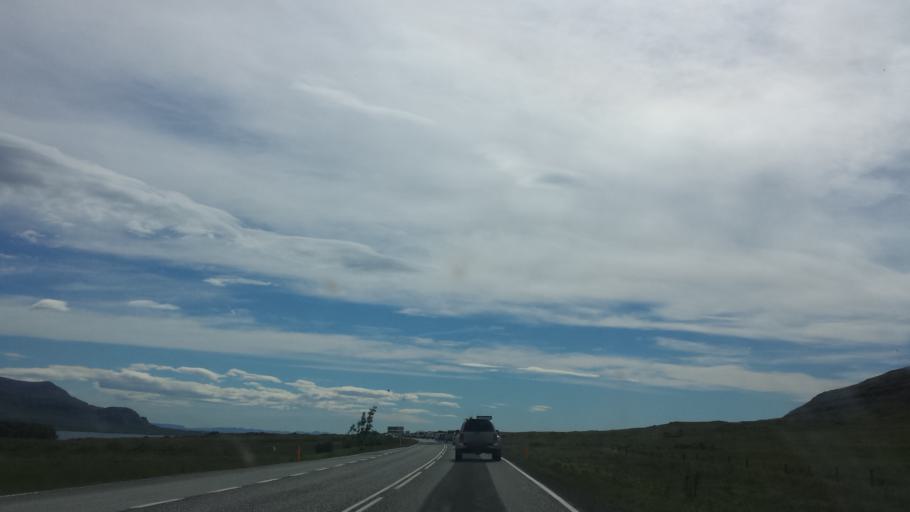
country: IS
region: Capital Region
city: Mosfellsbaer
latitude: 64.3513
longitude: -21.8100
